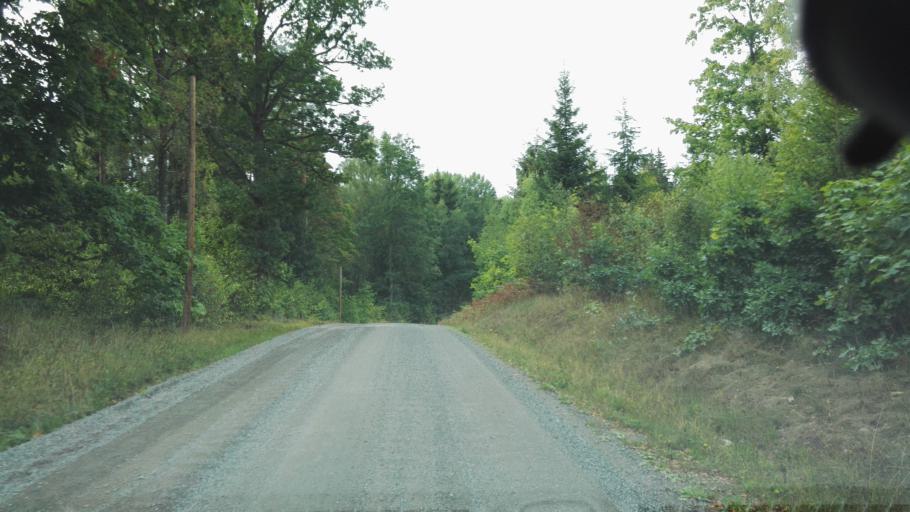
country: SE
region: Joenkoeping
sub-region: Vetlanda Kommun
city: Landsbro
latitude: 57.2117
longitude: 14.9211
